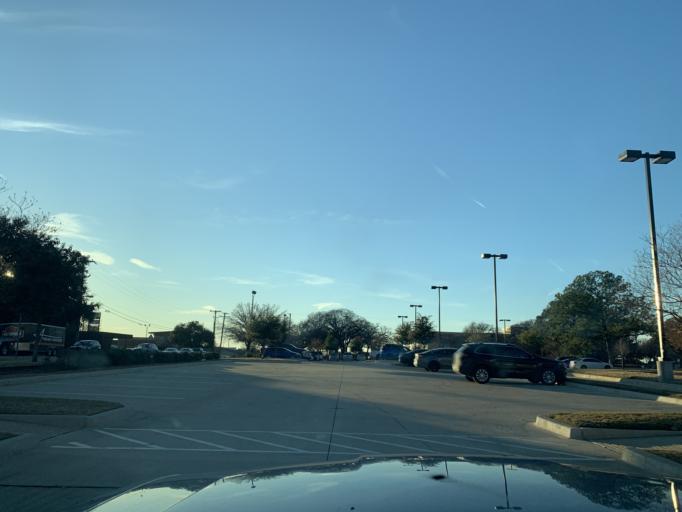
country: US
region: Texas
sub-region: Tarrant County
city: Bedford
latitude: 32.8384
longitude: -97.1359
